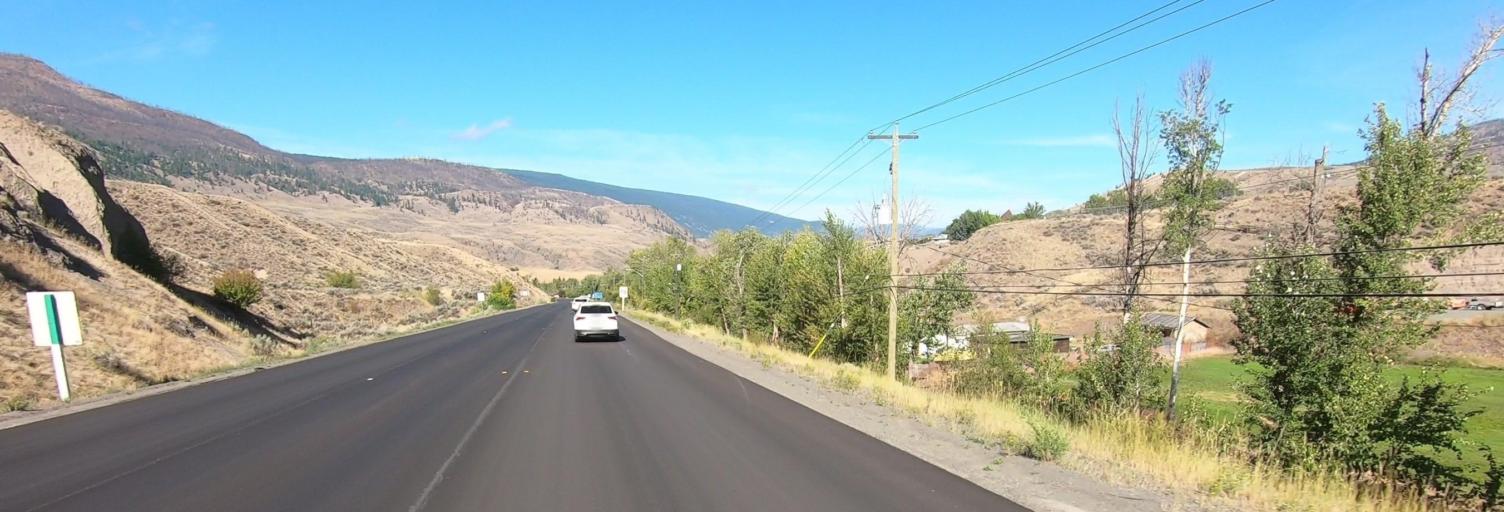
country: CA
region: British Columbia
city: Cache Creek
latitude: 50.8104
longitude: -121.3121
